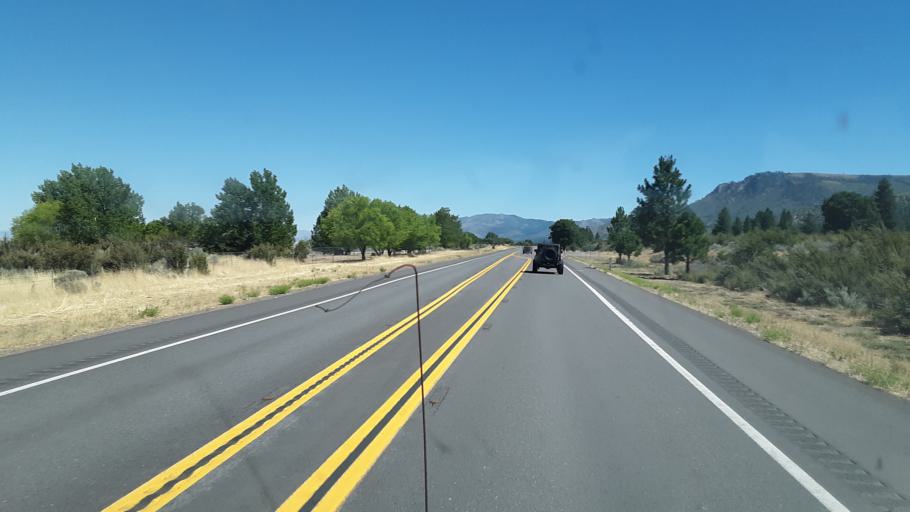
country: US
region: California
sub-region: Lassen County
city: Janesville
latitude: 40.2676
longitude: -120.4758
